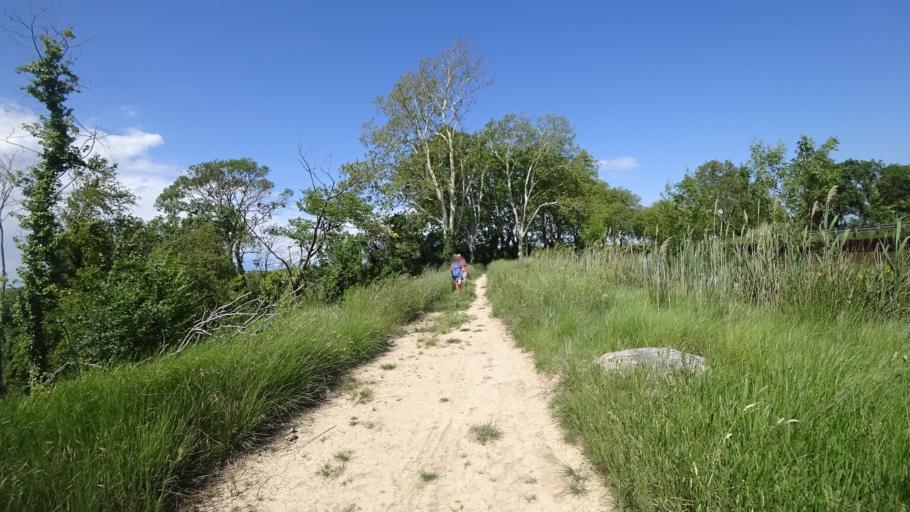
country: FR
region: Languedoc-Roussillon
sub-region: Departement de l'Aude
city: Ginestas
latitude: 43.2477
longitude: 2.8678
